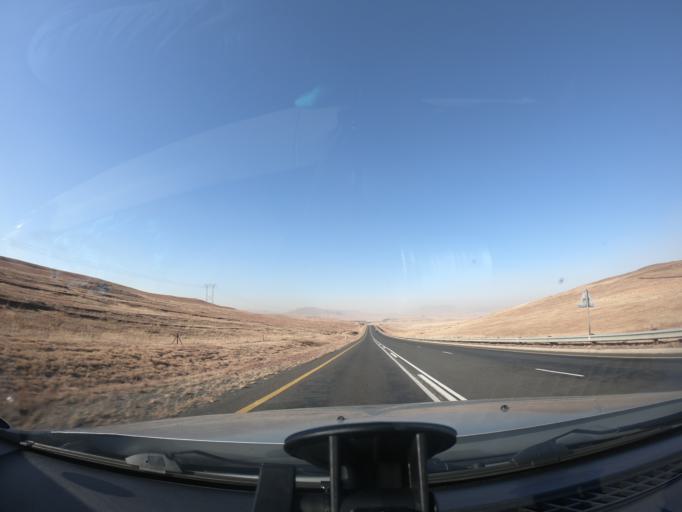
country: ZA
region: Mpumalanga
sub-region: Gert Sibande District Municipality
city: Volksrust
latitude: -27.2058
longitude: 29.8784
